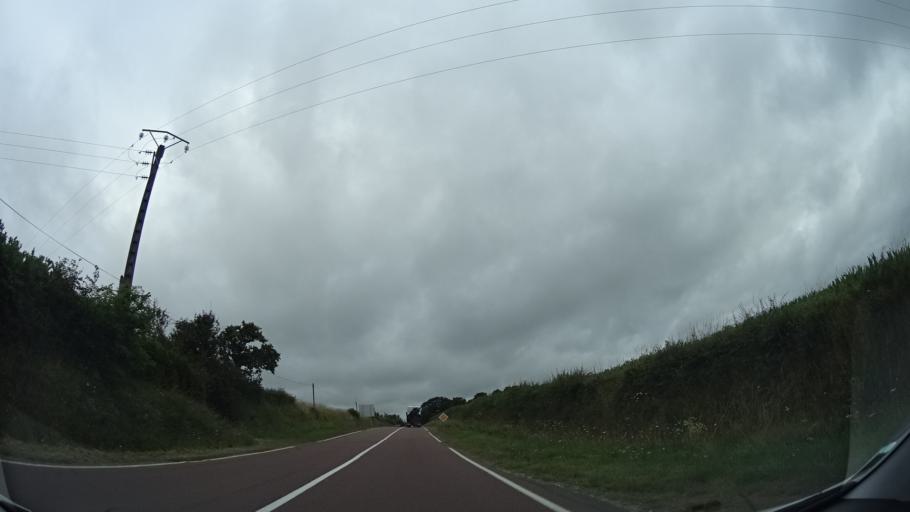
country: FR
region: Lower Normandy
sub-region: Departement de la Manche
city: Portbail
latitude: 49.3421
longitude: -1.6541
